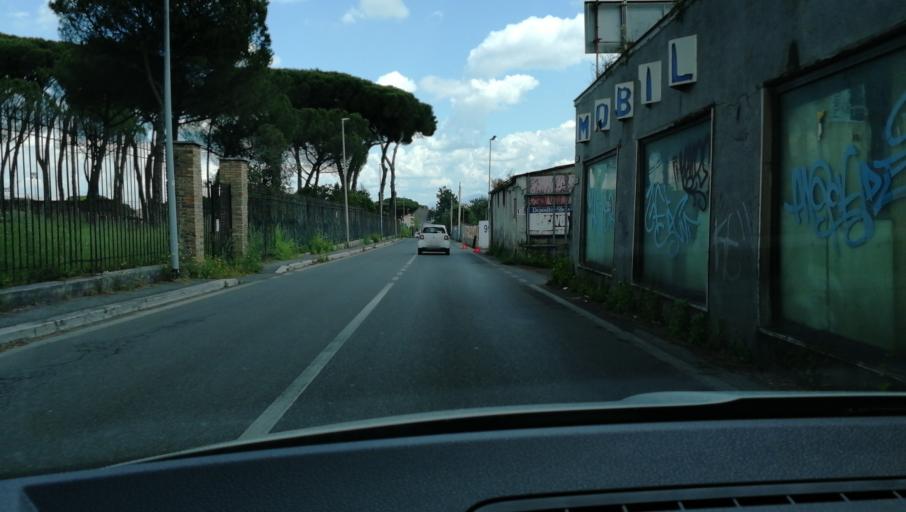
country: IT
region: Latium
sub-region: Citta metropolitana di Roma Capitale
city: Rome
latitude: 41.8605
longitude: 12.5373
